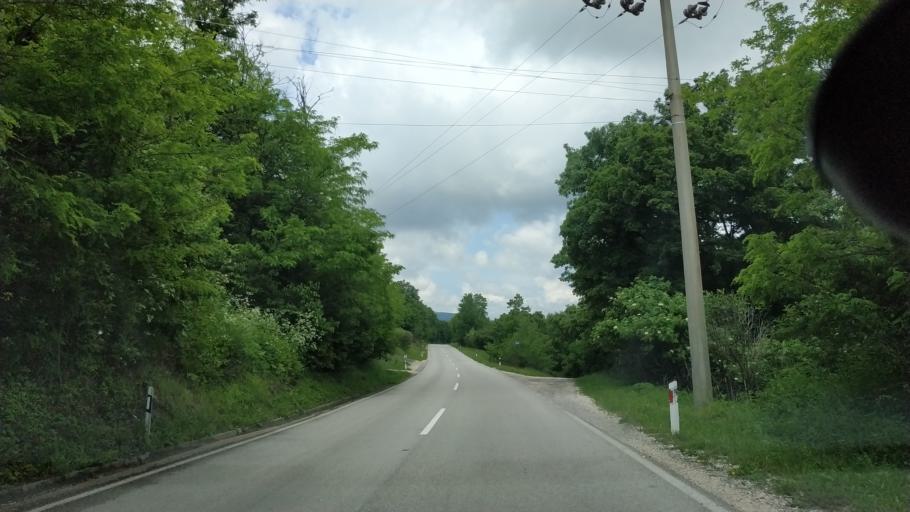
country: RS
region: Central Serbia
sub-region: Borski Okrug
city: Bor
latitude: 44.0743
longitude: 22.0263
